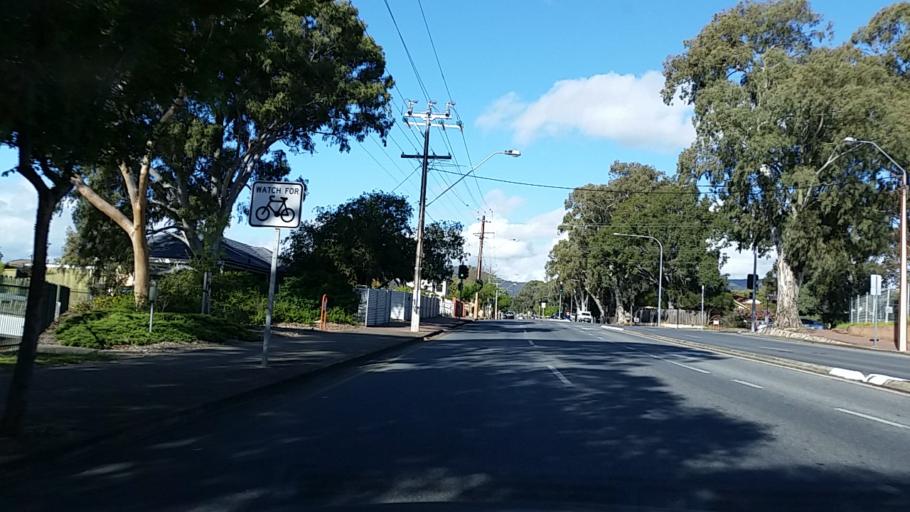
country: AU
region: South Australia
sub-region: Campbelltown
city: Hectorville
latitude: -34.8890
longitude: 138.6641
